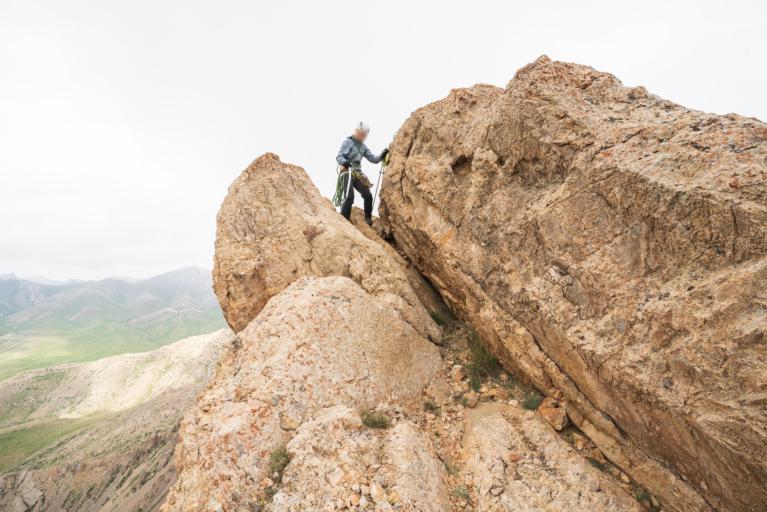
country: KZ
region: Ongtustik Qazaqstan
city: Ashchysay
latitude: 43.7445
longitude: 68.8356
